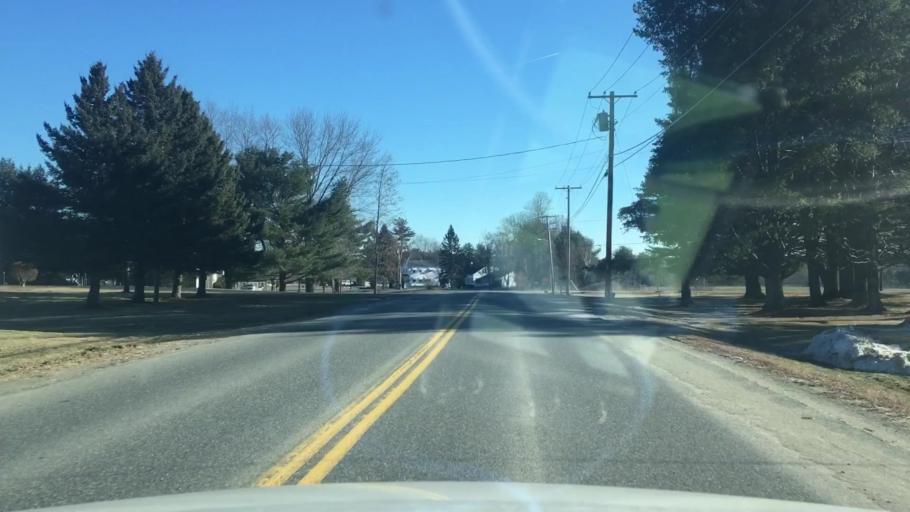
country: US
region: Maine
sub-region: Kennebec County
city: Winslow
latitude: 44.5446
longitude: -69.6070
